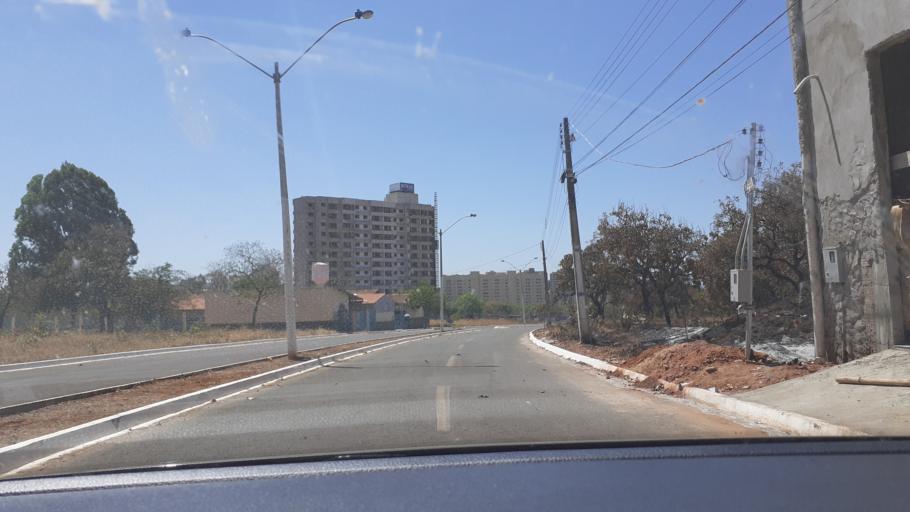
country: BR
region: Goias
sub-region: Caldas Novas
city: Caldas Novas
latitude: -17.7394
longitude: -48.6401
